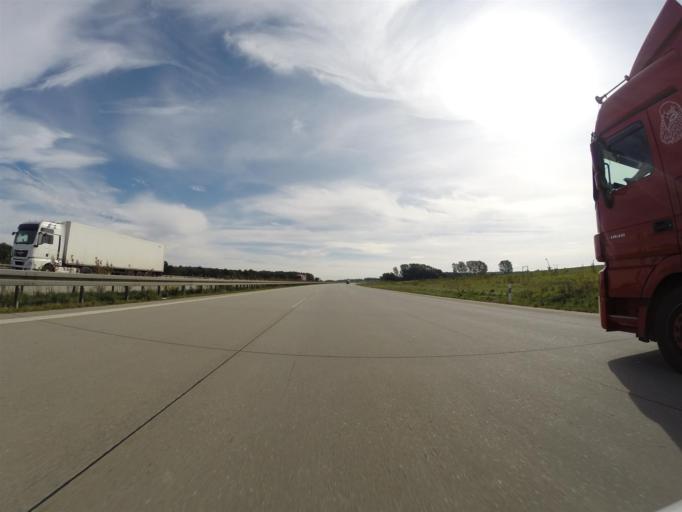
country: DE
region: Saxony
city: Remse
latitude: 50.8425
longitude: 12.5823
